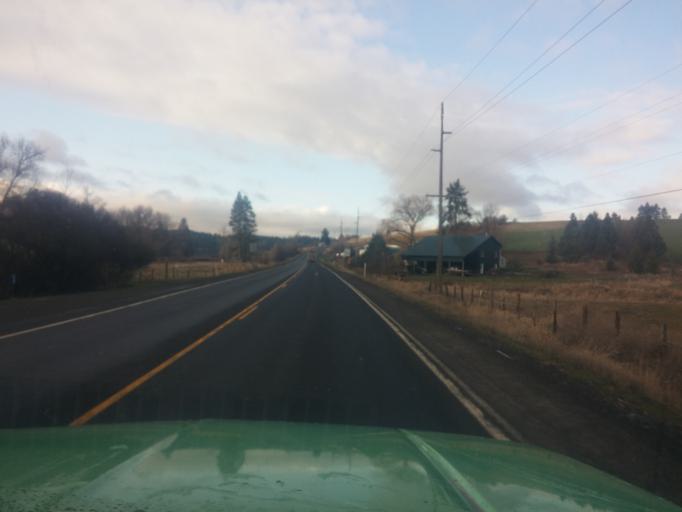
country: US
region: Idaho
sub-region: Latah County
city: Moscow
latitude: 46.9265
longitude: -116.9390
